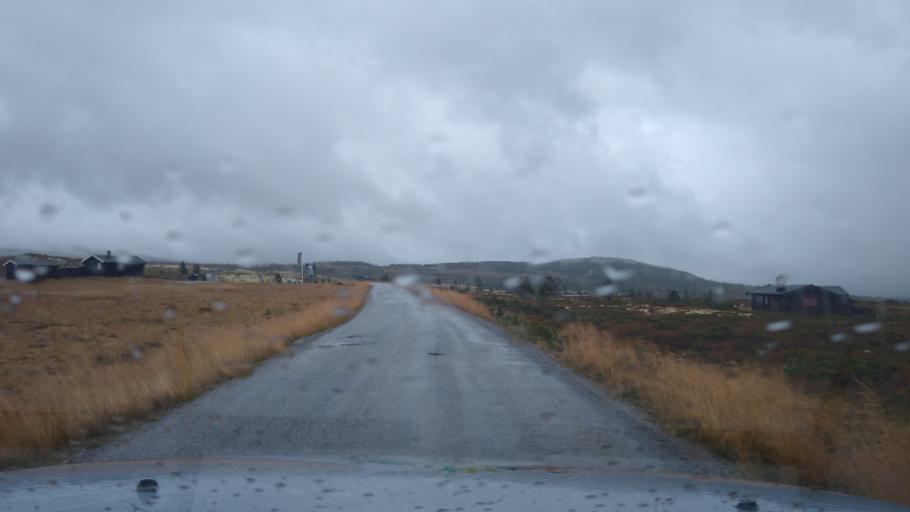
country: NO
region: Oppland
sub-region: Ringebu
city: Ringebu
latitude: 61.6705
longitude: 10.1144
